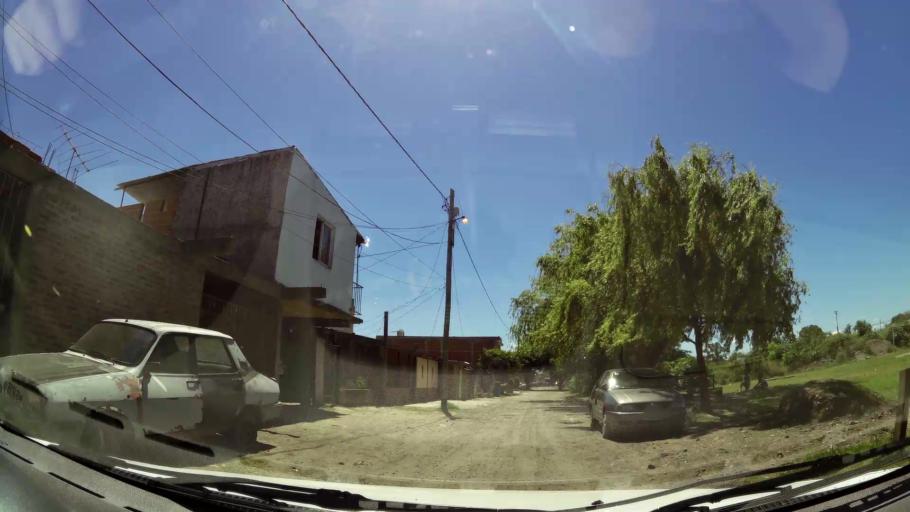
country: AR
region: Buenos Aires
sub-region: Partido de San Isidro
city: San Isidro
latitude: -34.5122
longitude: -58.5621
